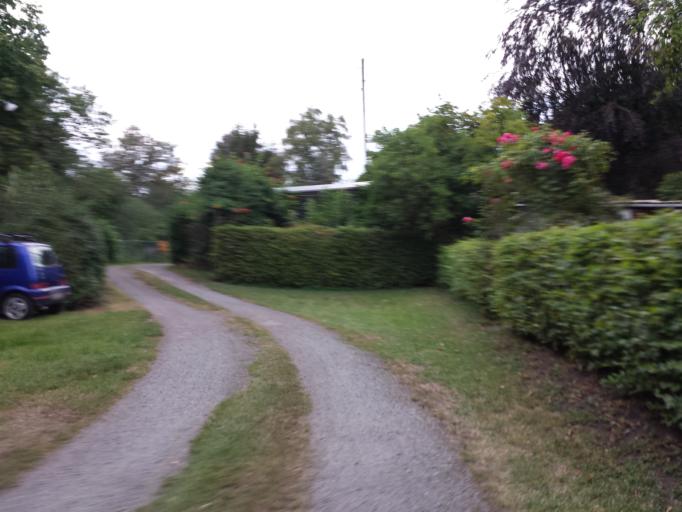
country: DE
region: Lower Saxony
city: Stuhr
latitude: 53.0650
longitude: 8.7665
